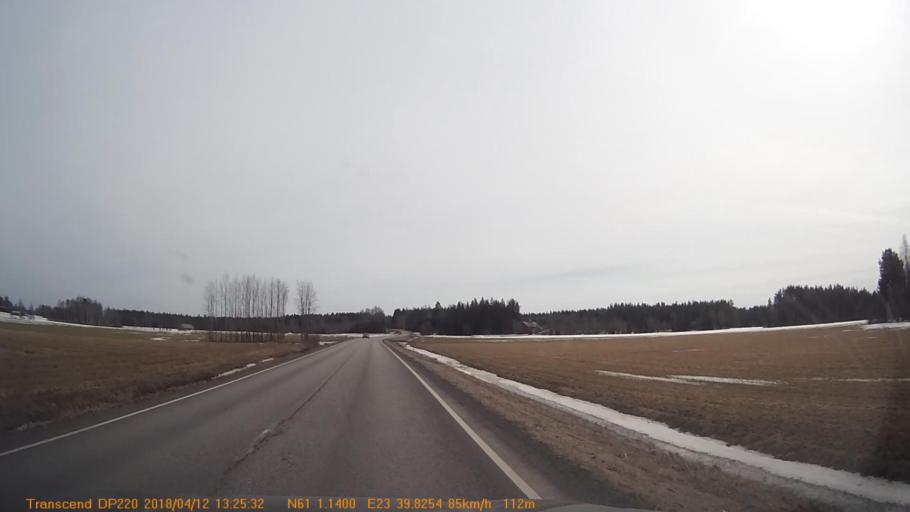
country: FI
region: Pirkanmaa
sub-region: Etelae-Pirkanmaa
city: Kylmaekoski
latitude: 61.0188
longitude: 23.6641
